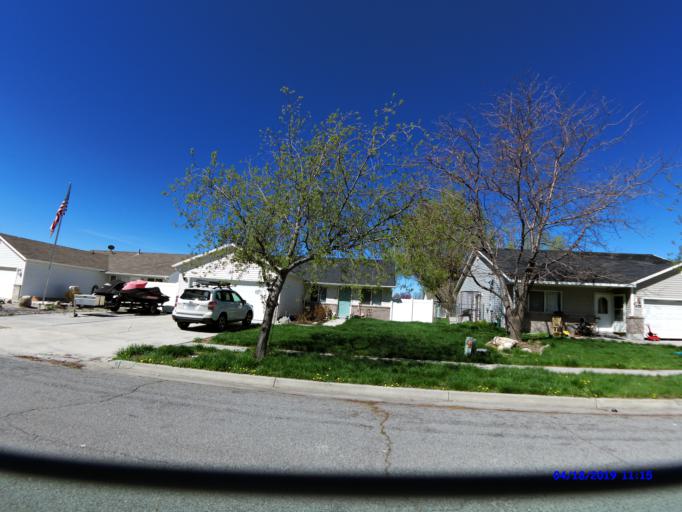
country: US
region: Utah
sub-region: Weber County
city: North Ogden
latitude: 41.2840
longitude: -111.9581
